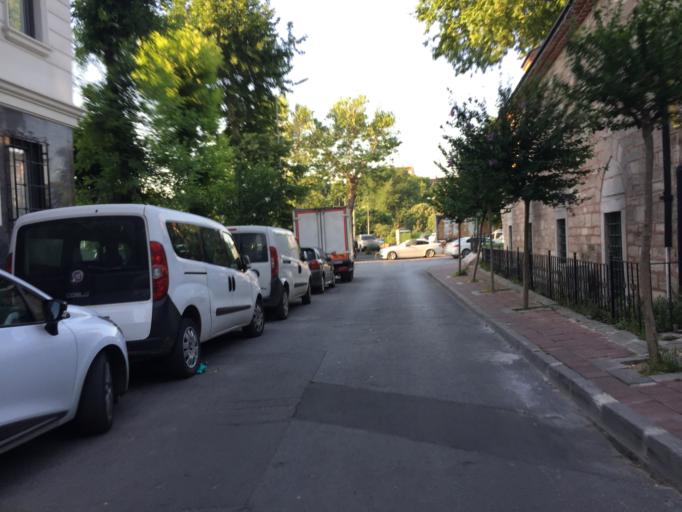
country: TR
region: Istanbul
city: Istanbul
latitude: 41.0153
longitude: 28.9401
